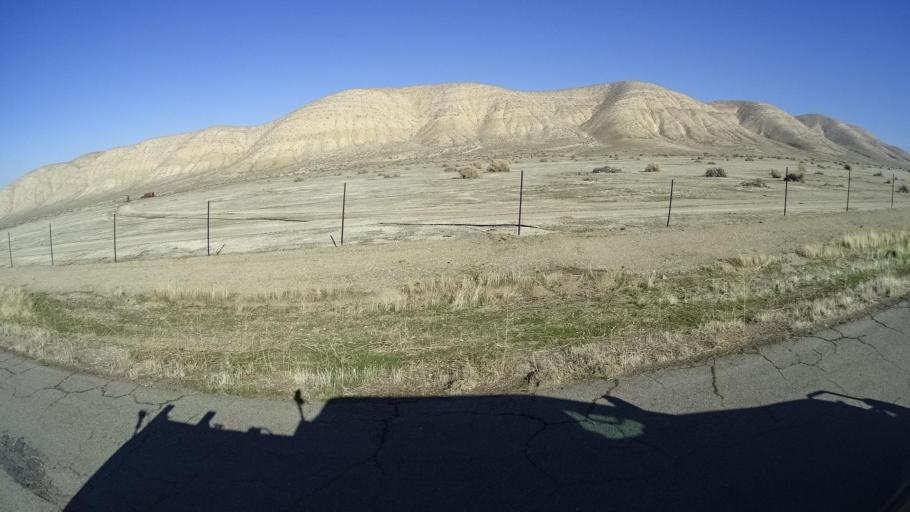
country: US
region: California
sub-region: Kern County
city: Maricopa
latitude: 35.0022
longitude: -119.4047
